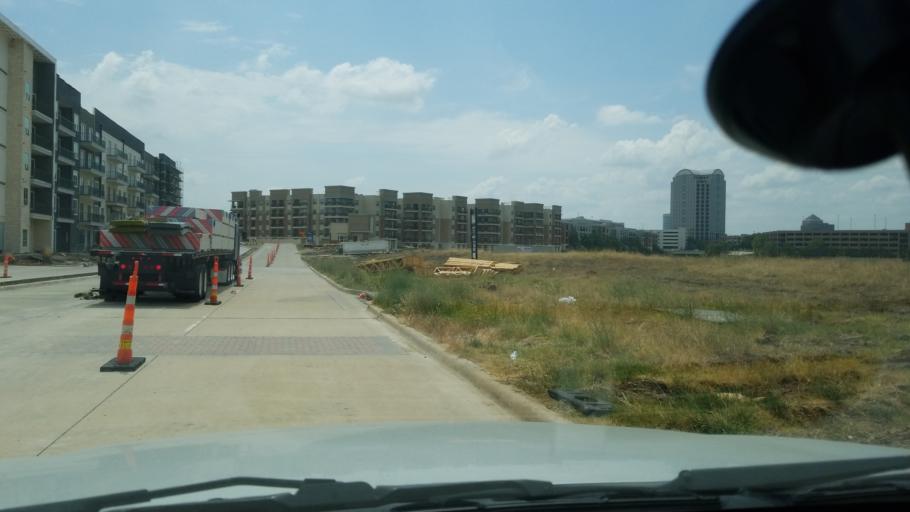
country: US
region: Texas
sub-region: Dallas County
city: Irving
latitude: 32.8752
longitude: -96.9387
